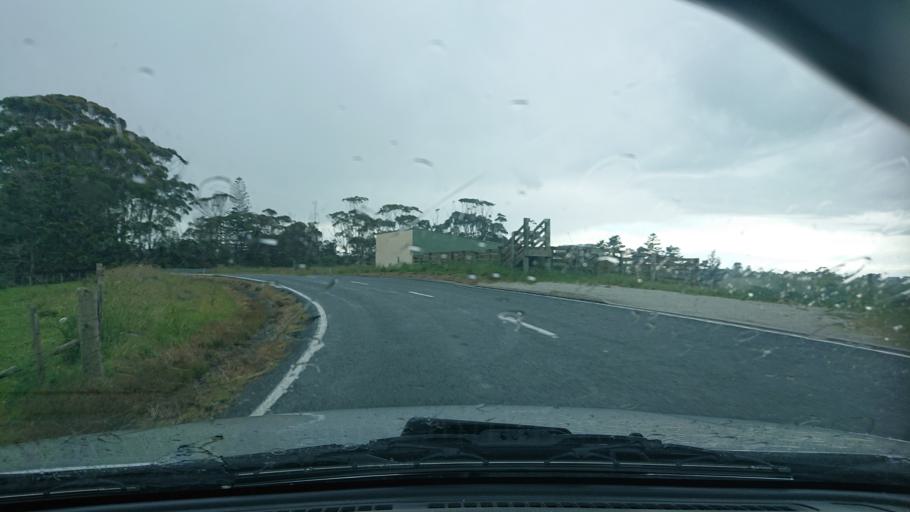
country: NZ
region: Auckland
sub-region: Auckland
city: Wellsford
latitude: -36.3310
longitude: 174.3871
